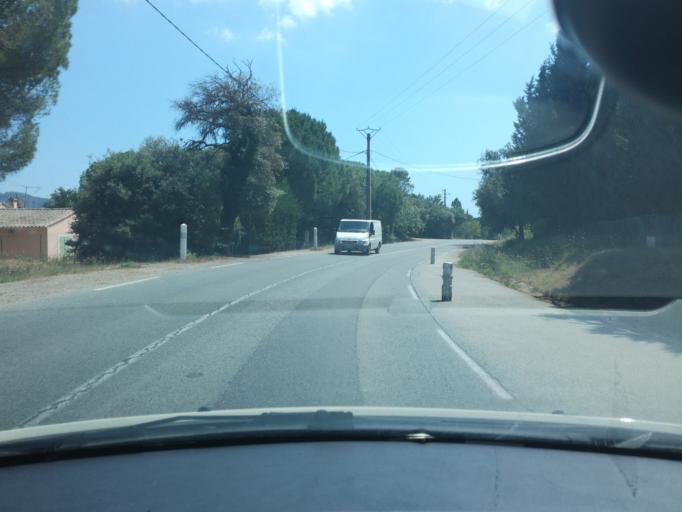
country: FR
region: Provence-Alpes-Cote d'Azur
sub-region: Departement du Var
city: Le Muy
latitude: 43.4860
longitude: 6.5674
